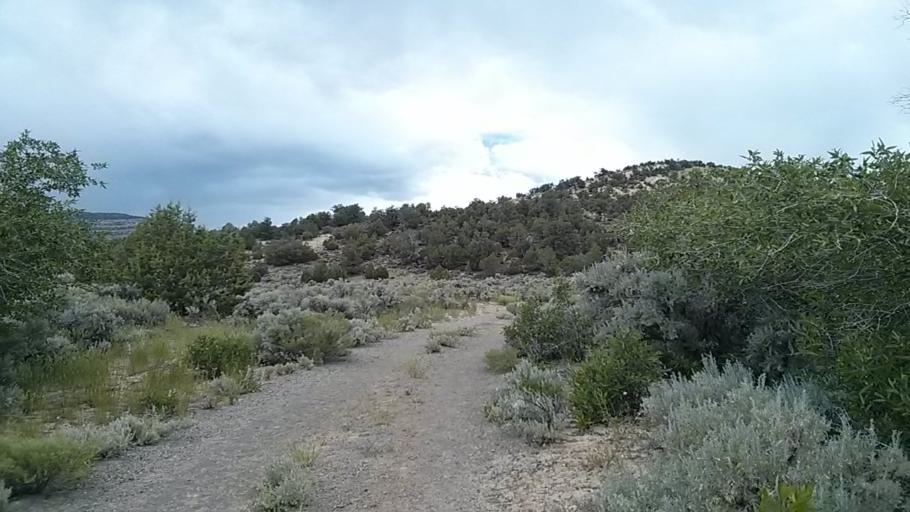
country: US
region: Utah
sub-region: Wayne County
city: Loa
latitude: 37.8628
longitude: -111.6366
